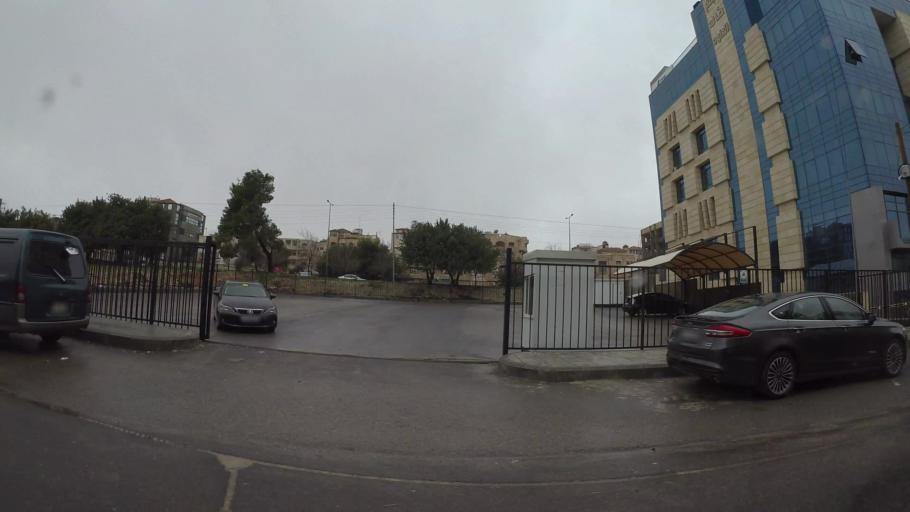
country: JO
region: Amman
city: Wadi as Sir
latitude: 31.9698
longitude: 35.8417
